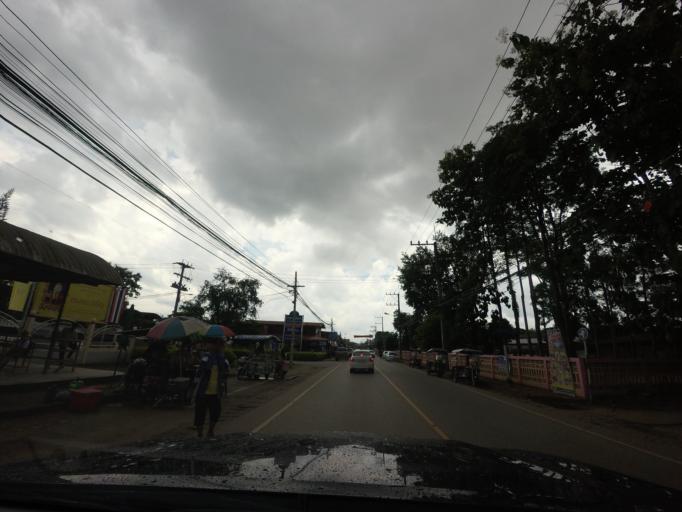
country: TH
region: Loei
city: Chiang Khan
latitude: 17.8958
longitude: 101.6631
